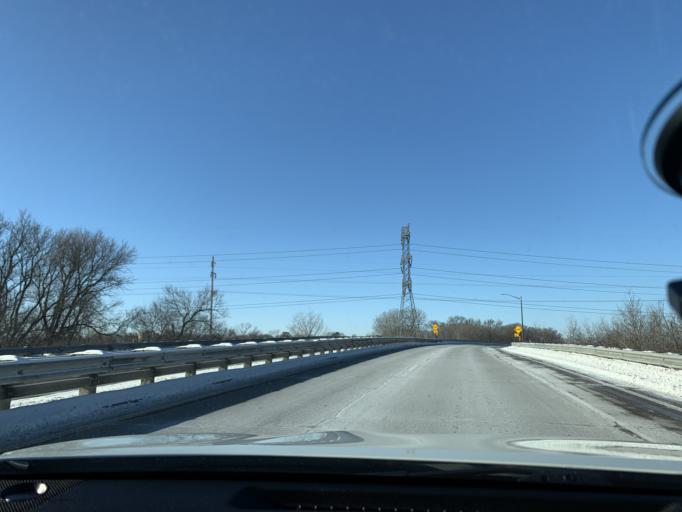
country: US
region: Minnesota
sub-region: Anoka County
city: Coon Rapids
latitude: 45.1463
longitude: -93.2893
